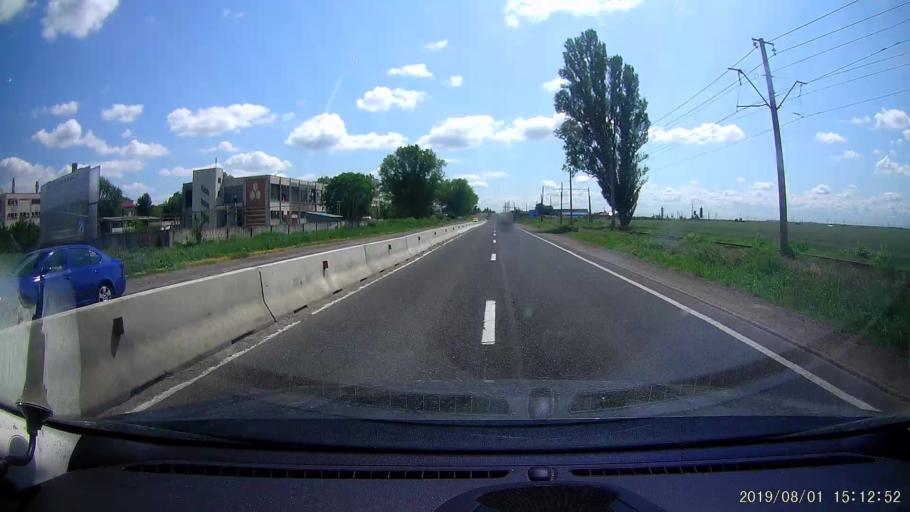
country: RO
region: Braila
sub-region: Comuna Chiscani
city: Lacu Sarat
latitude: 45.2002
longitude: 27.9070
